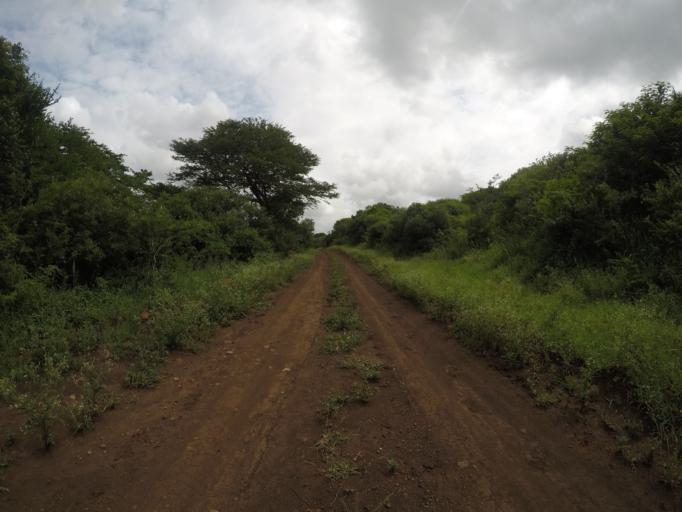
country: ZA
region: KwaZulu-Natal
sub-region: uThungulu District Municipality
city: Empangeni
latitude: -28.5928
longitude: 31.8743
